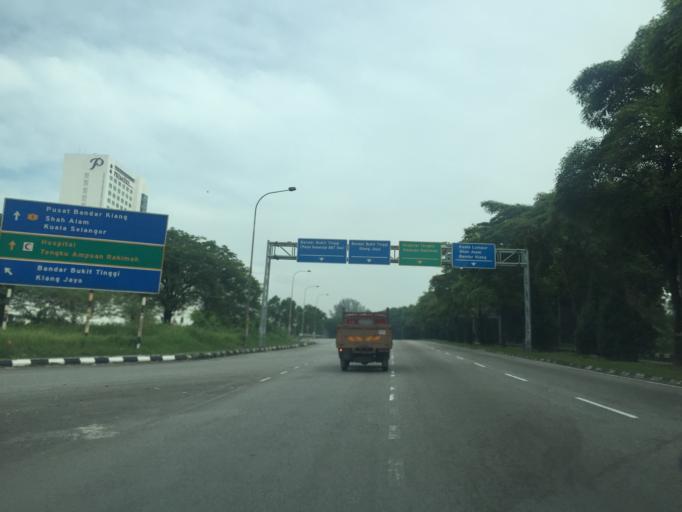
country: MY
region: Selangor
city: Klang
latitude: 3.0047
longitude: 101.4421
